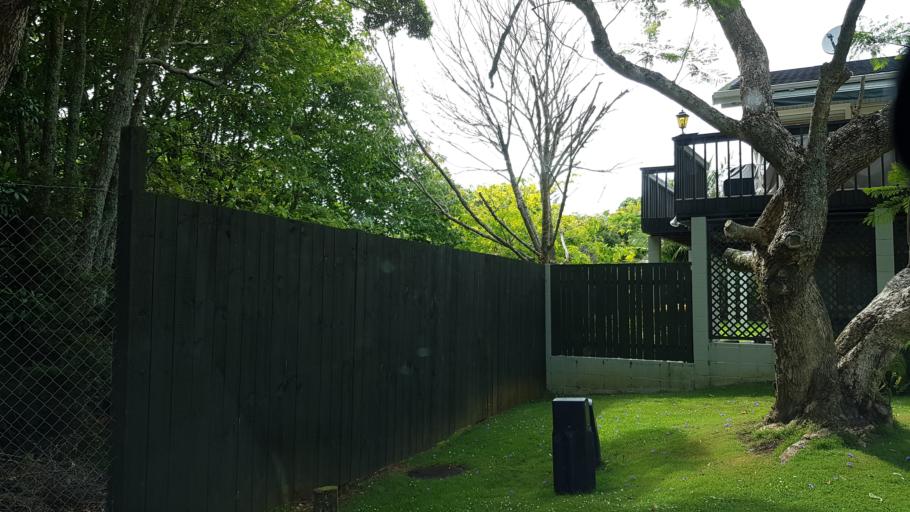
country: NZ
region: Auckland
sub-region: Auckland
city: North Shore
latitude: -36.7871
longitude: 174.7454
